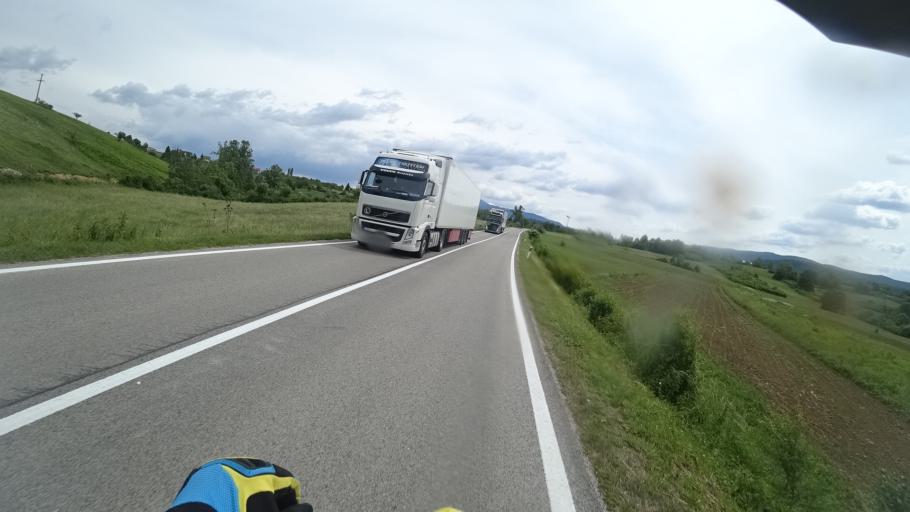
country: BA
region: Federation of Bosnia and Herzegovina
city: Izacic
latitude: 44.9134
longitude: 15.7189
